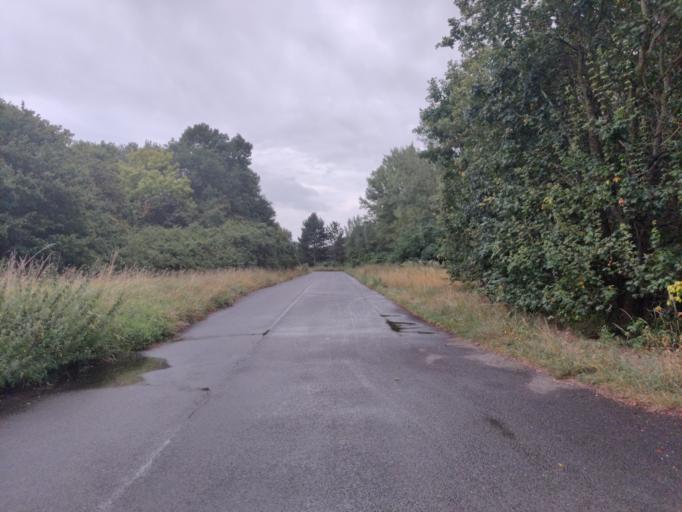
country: AT
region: Lower Austria
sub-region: Politischer Bezirk Korneuburg
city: Langenzersdorf
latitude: 48.2966
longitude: 16.3475
